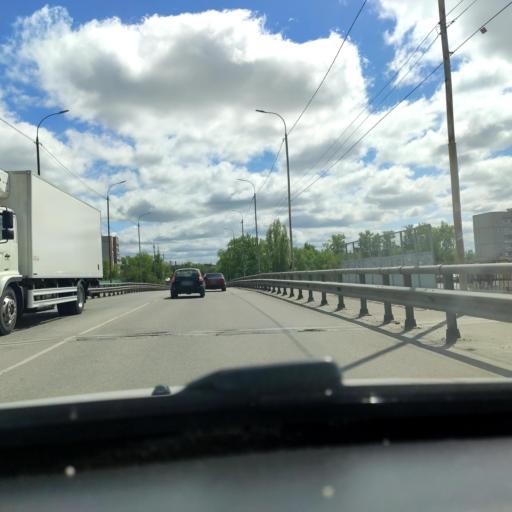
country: RU
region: Voronezj
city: Voronezh
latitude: 51.7266
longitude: 39.2614
